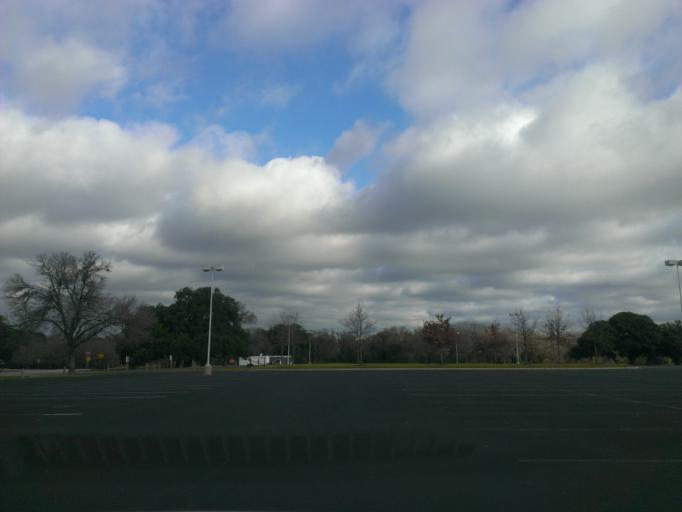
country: US
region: Texas
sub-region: Williamson County
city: Round Rock
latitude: 30.5276
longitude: -97.6326
